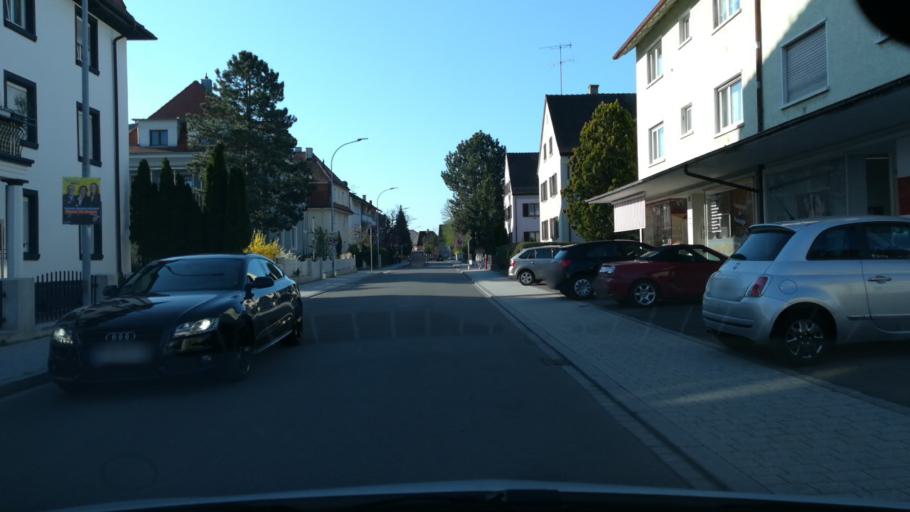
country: DE
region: Baden-Wuerttemberg
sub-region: Freiburg Region
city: Singen
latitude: 47.7683
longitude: 8.8408
